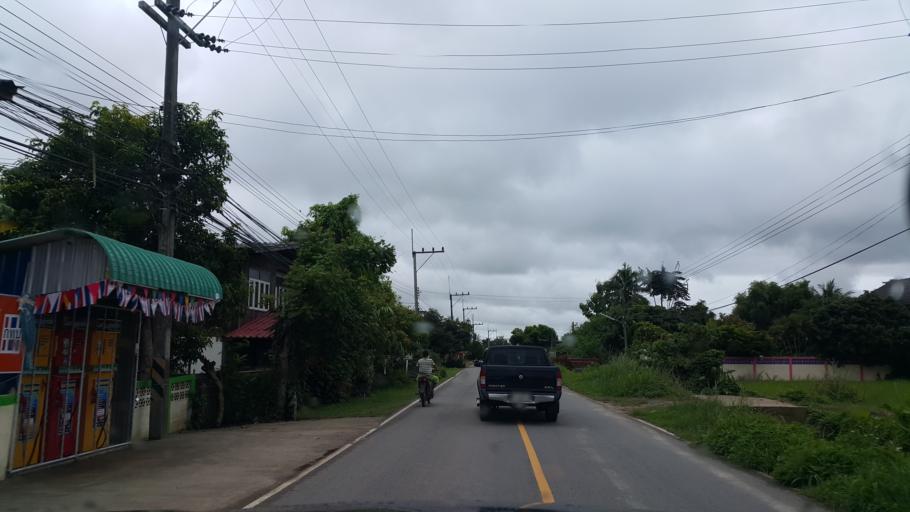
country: TH
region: Phayao
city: Chiang Kham
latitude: 19.5232
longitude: 100.3377
